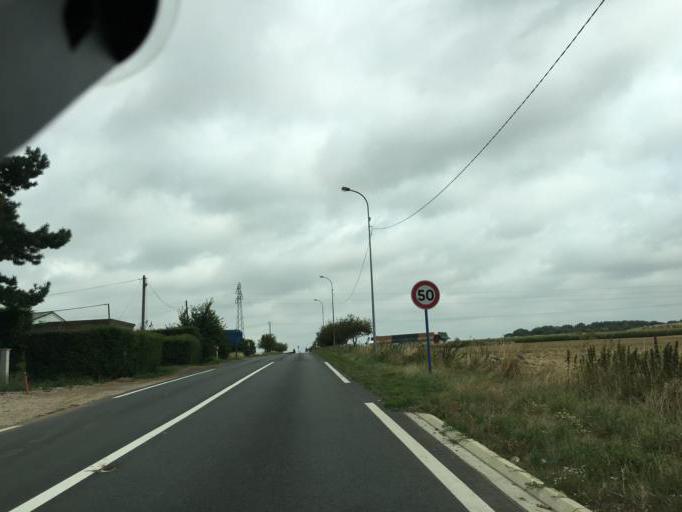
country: FR
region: Nord-Pas-de-Calais
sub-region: Departement du Pas-de-Calais
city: Saint-Pol-sur-Ternoise
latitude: 50.3882
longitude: 2.3504
